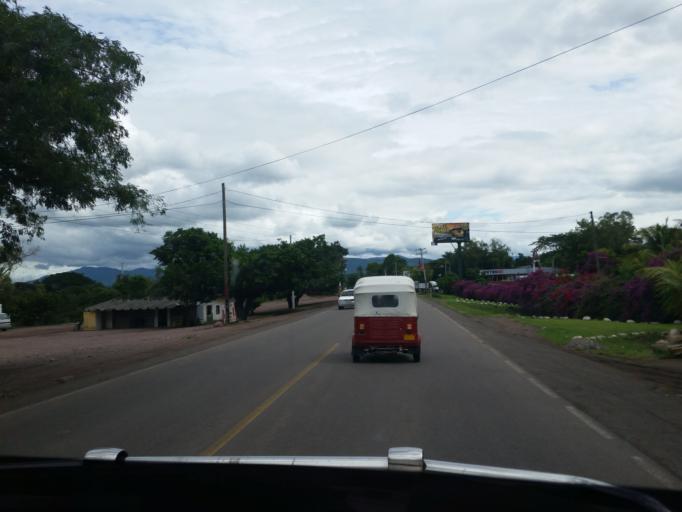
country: NI
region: Matagalpa
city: Ciudad Dario
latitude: 12.8425
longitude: -86.1039
